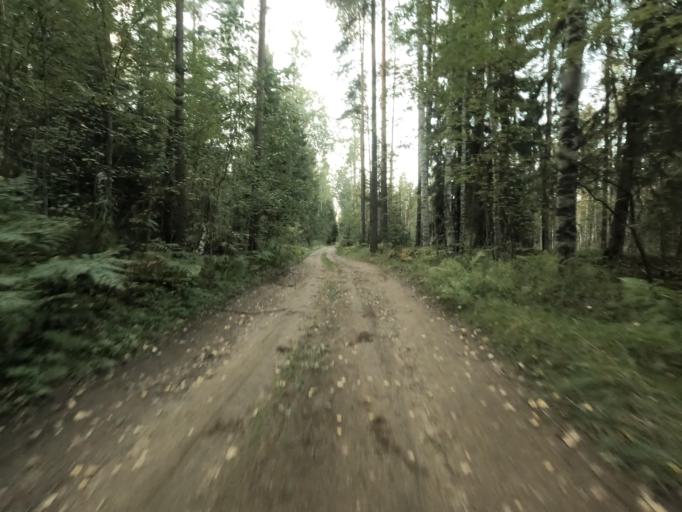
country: RU
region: Leningrad
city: Otradnoye
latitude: 59.8352
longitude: 30.8080
